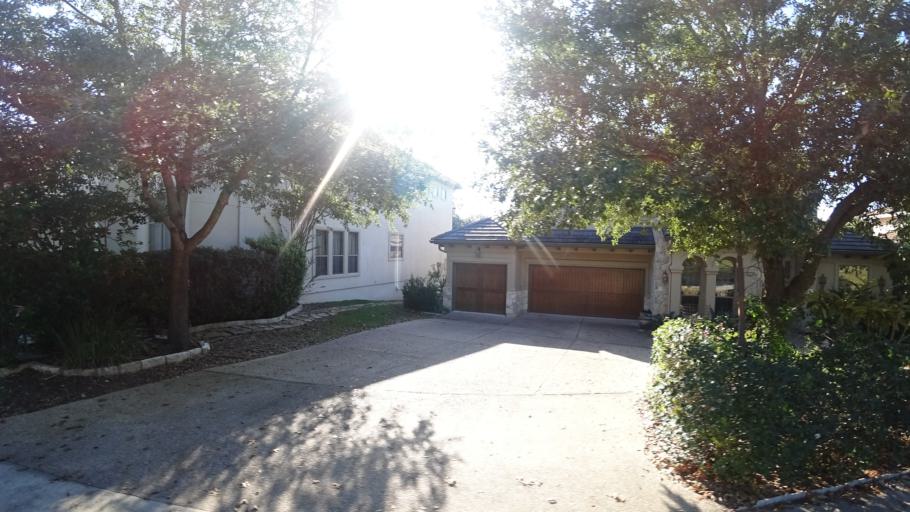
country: US
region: Texas
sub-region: Travis County
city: Hudson Bend
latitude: 30.3569
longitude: -97.8905
